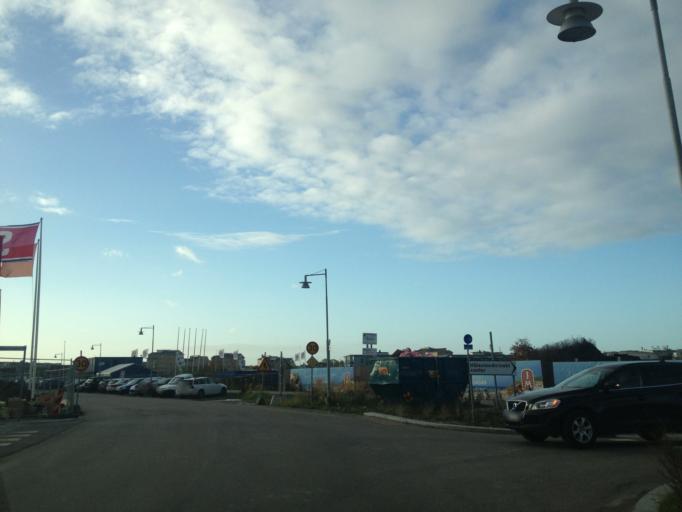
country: SE
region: Skane
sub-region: Lomma Kommun
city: Lomma
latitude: 55.6786
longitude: 13.0667
